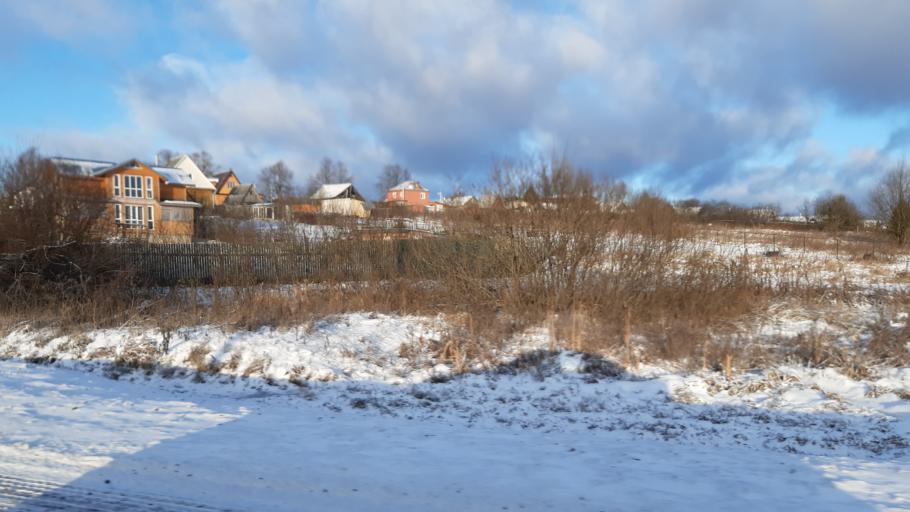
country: RU
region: Moskovskaya
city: Svatkovo
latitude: 56.3098
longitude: 38.3214
